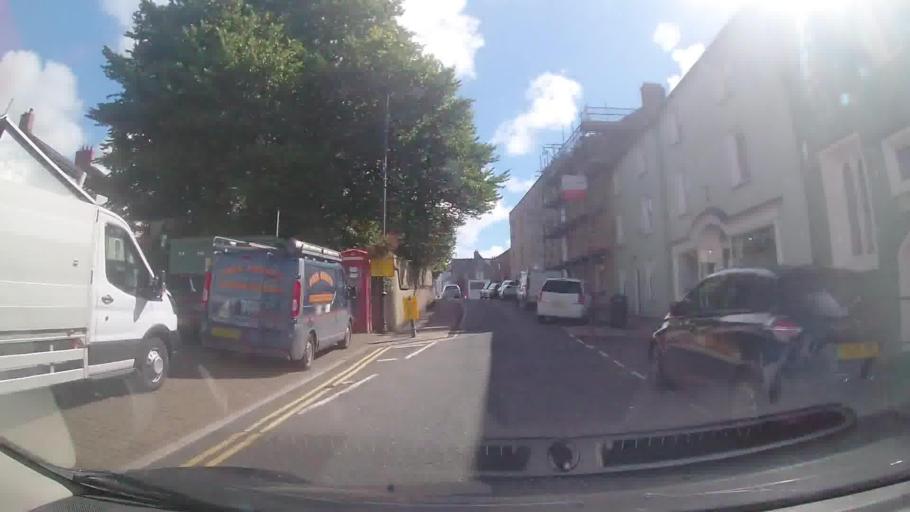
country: GB
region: Wales
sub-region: Pembrokeshire
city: Pembroke
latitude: 51.6750
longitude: -4.9140
